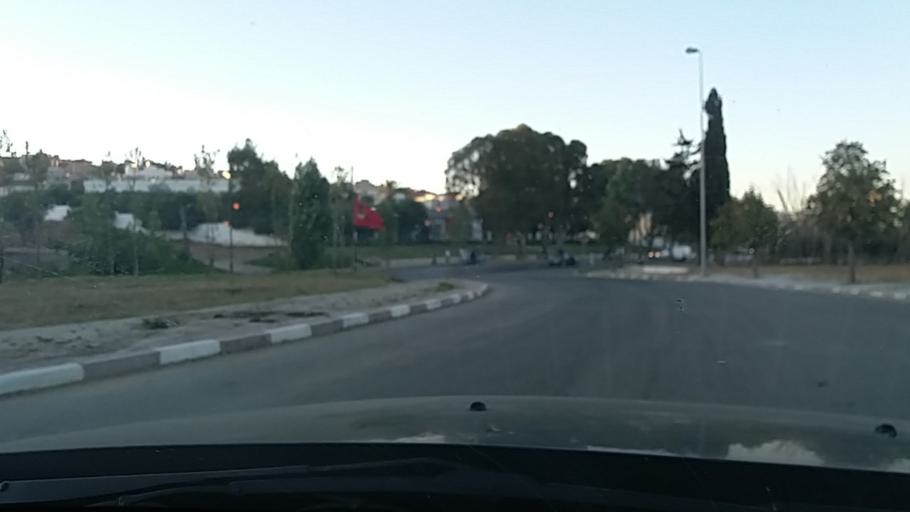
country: MA
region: Tanger-Tetouan
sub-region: Tanger-Assilah
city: Boukhalef
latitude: 35.7445
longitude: -5.8627
